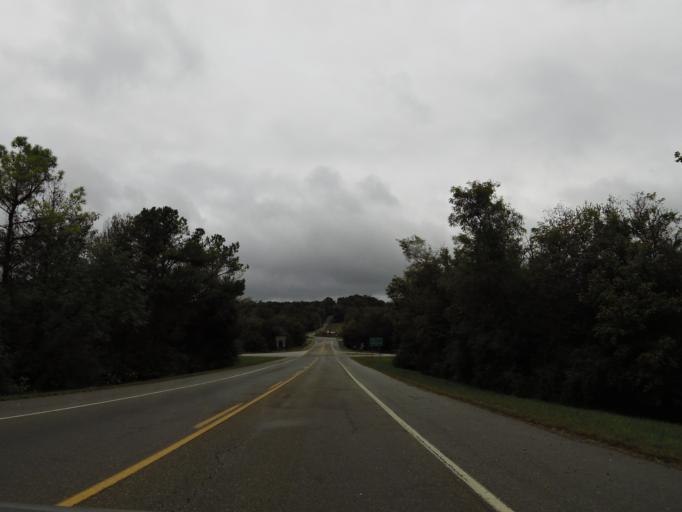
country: US
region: Tennessee
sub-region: Loudon County
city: Loudon
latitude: 35.7841
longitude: -84.3448
